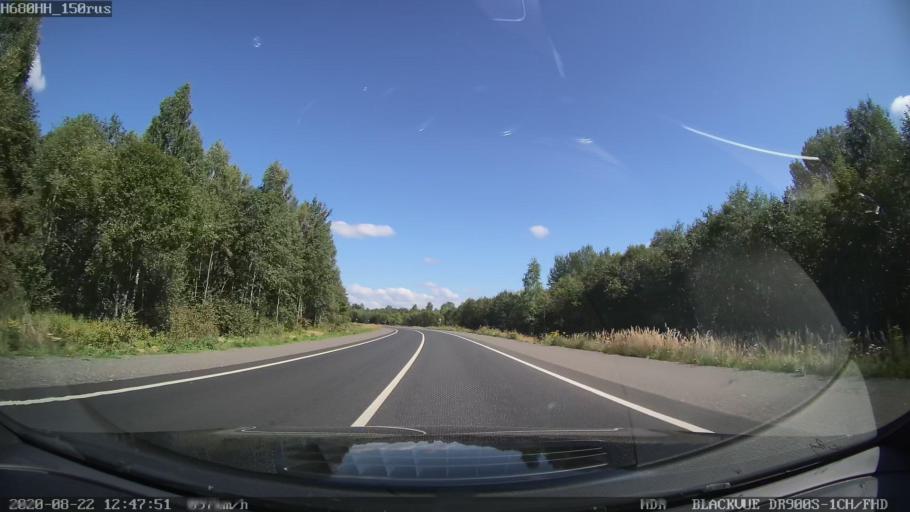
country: RU
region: Tverskaya
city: Rameshki
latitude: 57.4324
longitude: 36.1764
